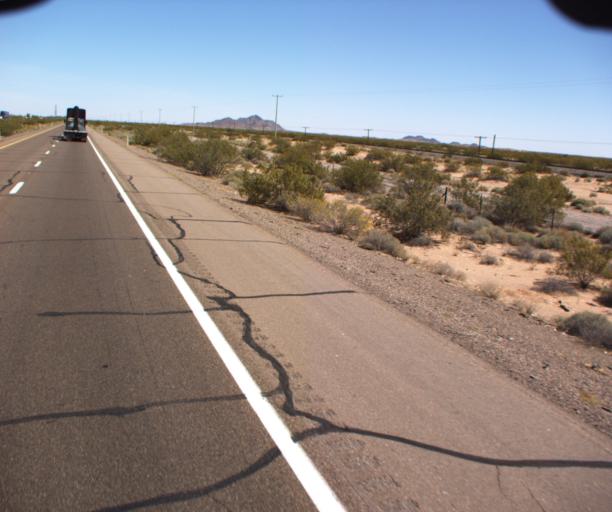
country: US
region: Arizona
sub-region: Yuma County
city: Wellton
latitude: 32.7842
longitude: -113.5734
